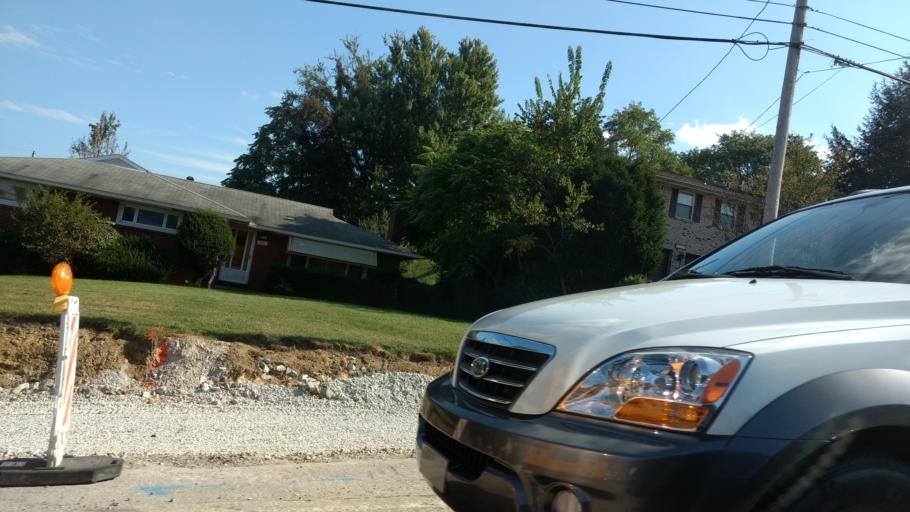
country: US
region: Pennsylvania
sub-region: Washington County
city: Wickerham Manor-Fisher
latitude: 40.1714
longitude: -79.9165
